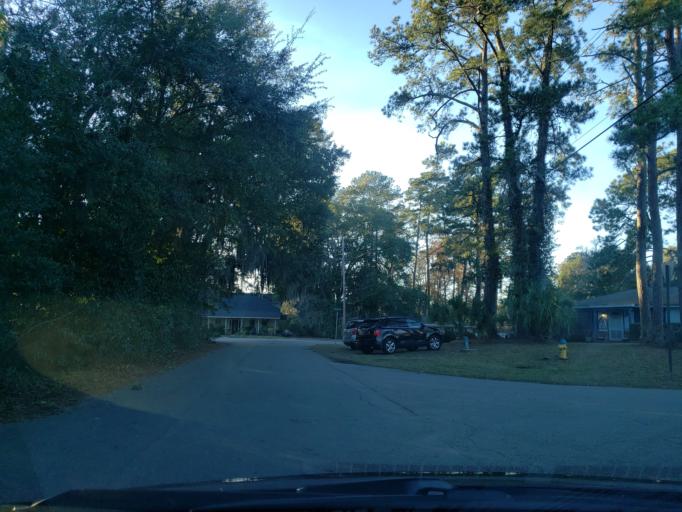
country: US
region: Georgia
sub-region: Chatham County
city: Isle of Hope
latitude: 31.9920
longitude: -81.1110
